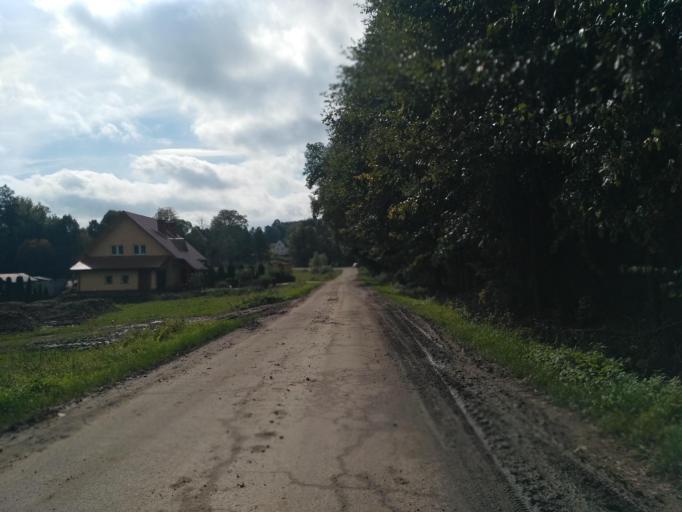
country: PL
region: Subcarpathian Voivodeship
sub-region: Powiat ropczycko-sedziszowski
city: Niedzwiada
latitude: 49.9323
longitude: 21.5378
